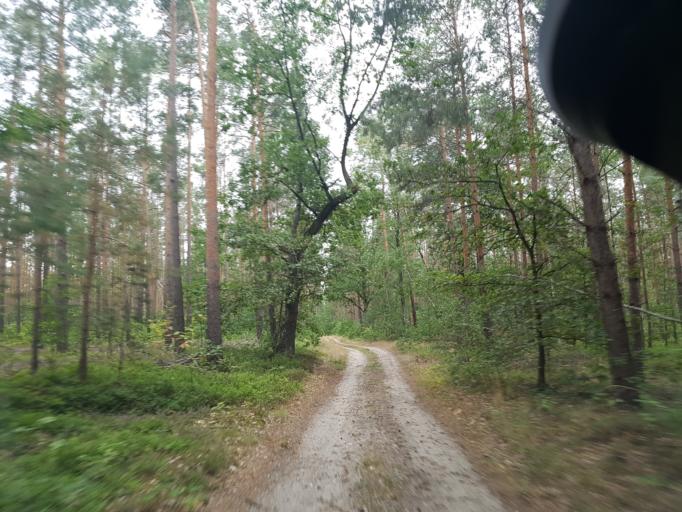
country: DE
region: Brandenburg
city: Ruckersdorf
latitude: 51.5982
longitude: 13.5710
